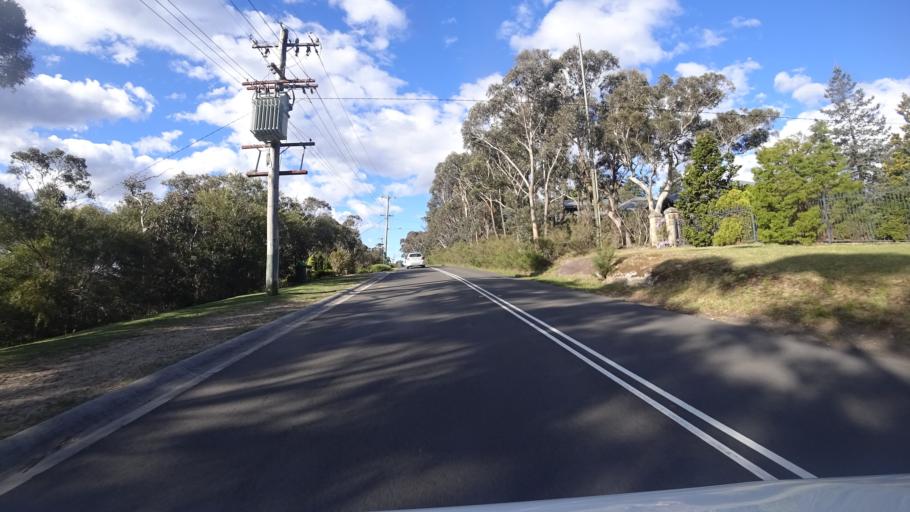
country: AU
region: New South Wales
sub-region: Blue Mountains Municipality
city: Katoomba
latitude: -33.7181
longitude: 150.2947
